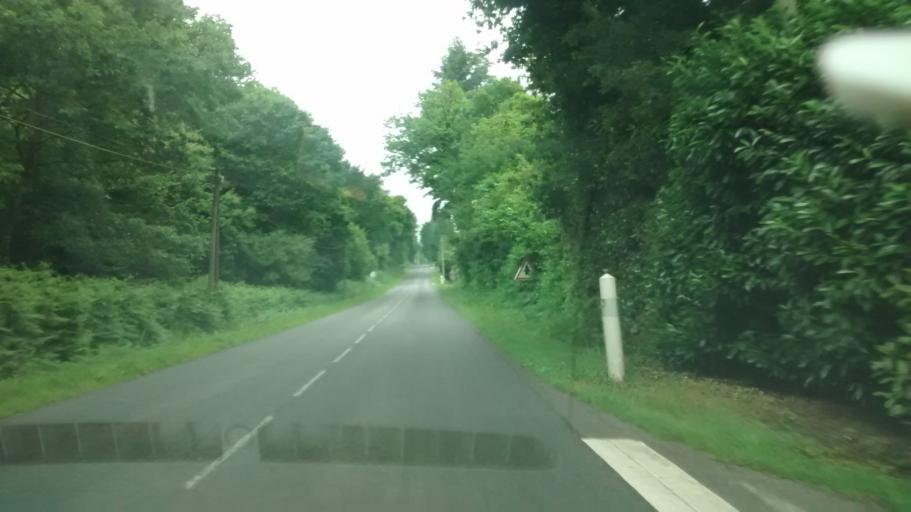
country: FR
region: Brittany
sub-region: Departement du Morbihan
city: Serent
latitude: 47.8194
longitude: -2.4750
